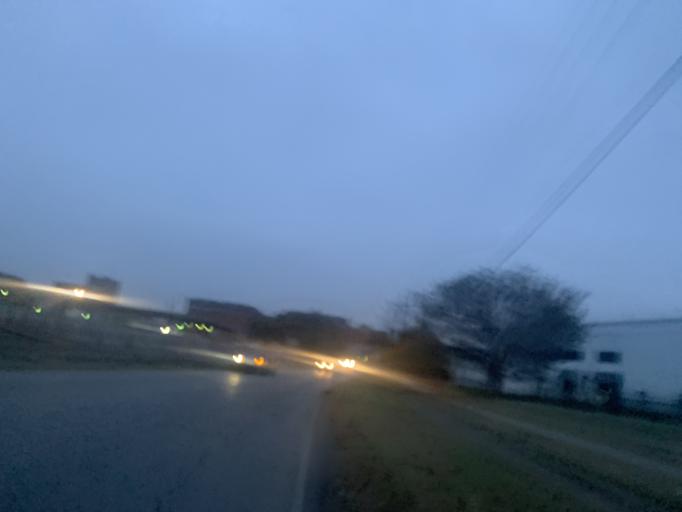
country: US
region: Kentucky
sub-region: Jefferson County
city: Shively
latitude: 38.2160
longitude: -85.7883
